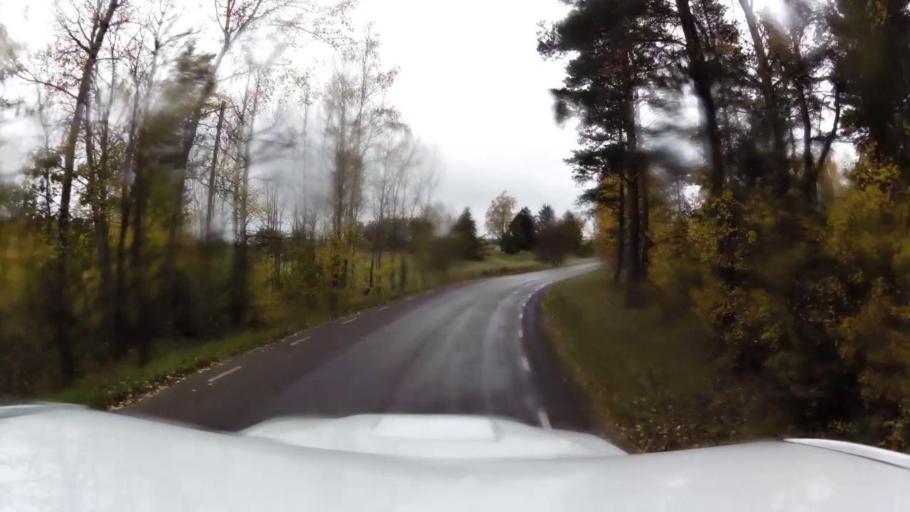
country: SE
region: OEstergoetland
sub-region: Linkopings Kommun
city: Linghem
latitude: 58.4631
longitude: 15.8261
